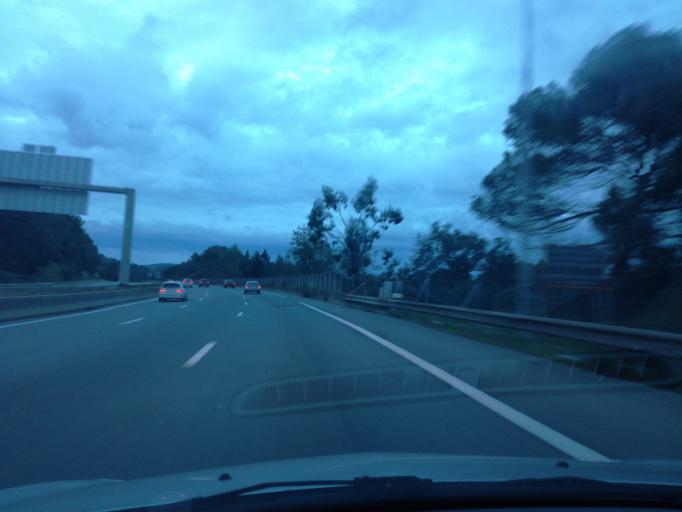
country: FR
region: Provence-Alpes-Cote d'Azur
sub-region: Departement du Var
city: Frejus
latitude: 43.4782
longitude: 6.7423
